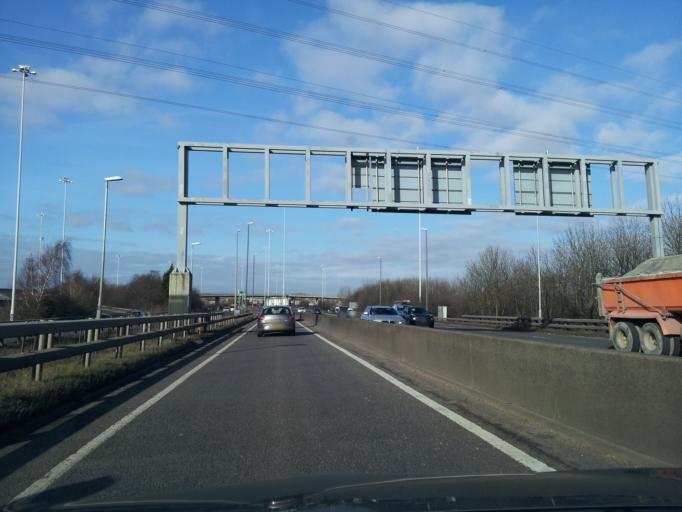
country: GB
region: England
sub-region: Nottingham
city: Nottingham
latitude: 52.9260
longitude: -1.1665
